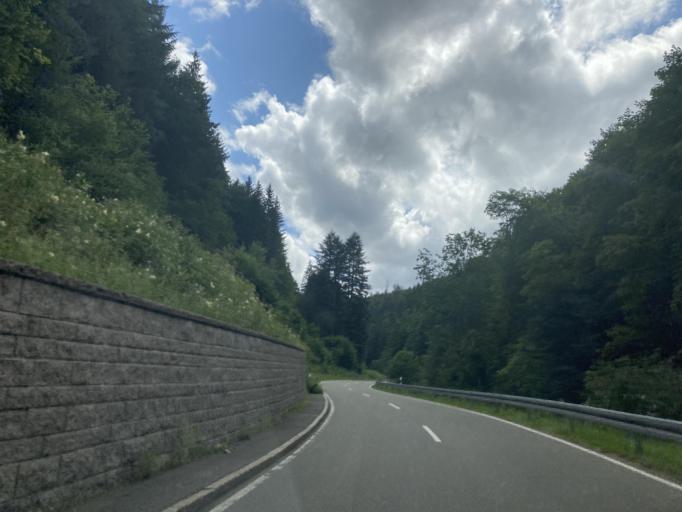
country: DE
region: Baden-Wuerttemberg
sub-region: Freiburg Region
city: Schonach im Schwarzwald
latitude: 48.1698
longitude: 8.1592
